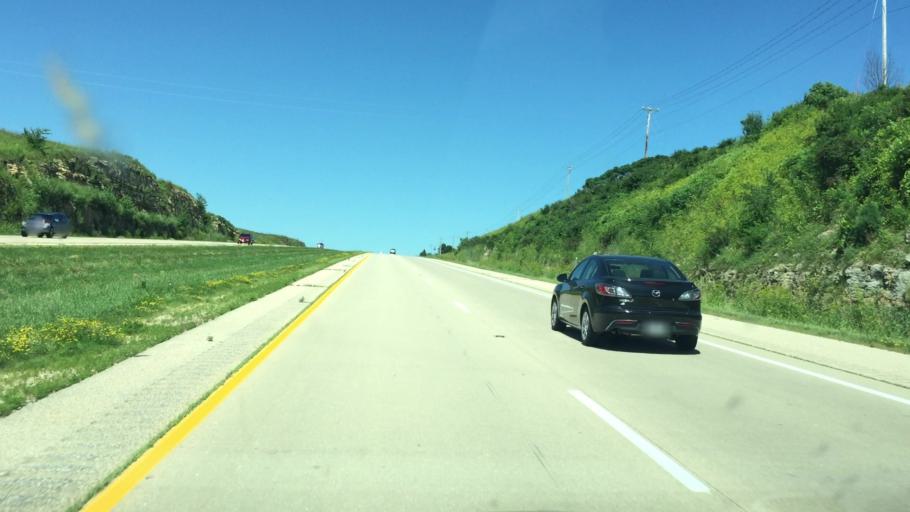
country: US
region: Wisconsin
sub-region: Iowa County
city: Mineral Point
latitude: 42.8284
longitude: -90.2346
